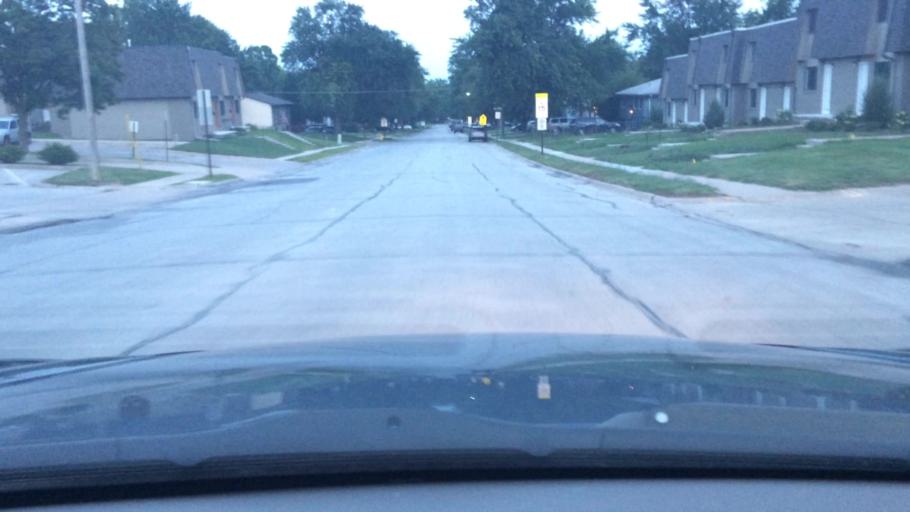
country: US
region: Nebraska
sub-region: Sarpy County
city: La Vista
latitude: 41.1870
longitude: -96.0393
